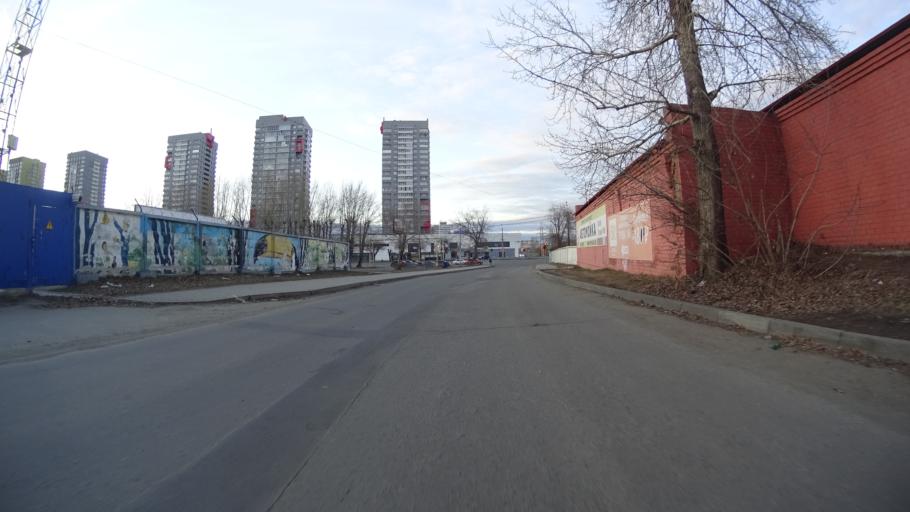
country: RU
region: Chelyabinsk
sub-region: Gorod Chelyabinsk
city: Chelyabinsk
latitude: 55.1697
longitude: 61.3703
